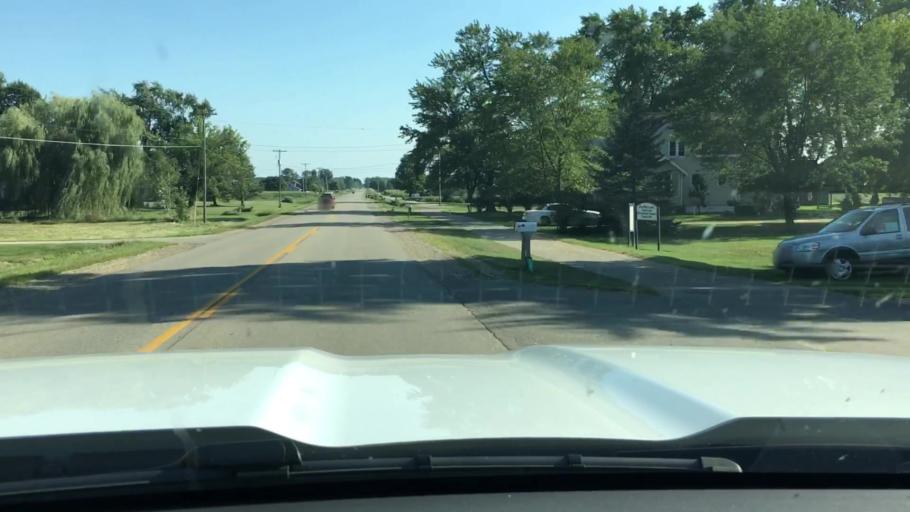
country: US
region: Michigan
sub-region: Ottawa County
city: Zeeland
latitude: 42.8008
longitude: -85.9401
